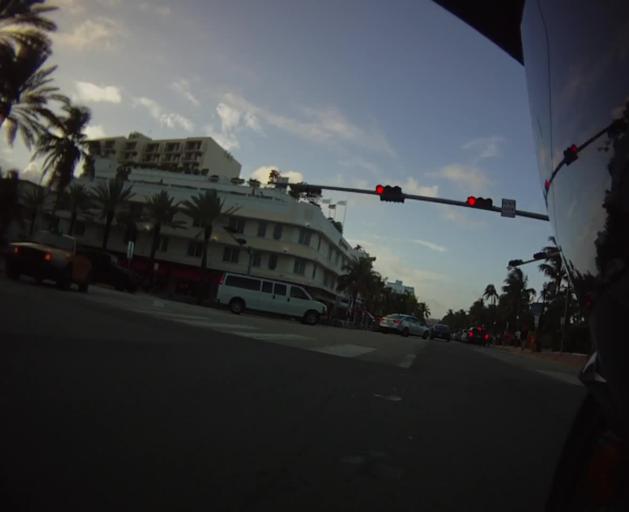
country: US
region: Florida
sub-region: Miami-Dade County
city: Miami Beach
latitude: 25.7744
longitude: -80.1320
